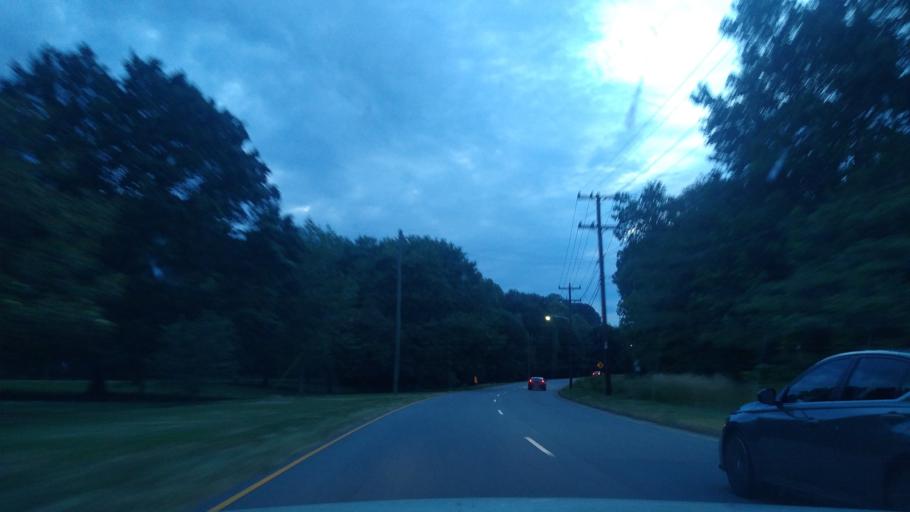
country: US
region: North Carolina
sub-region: Guilford County
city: Greensboro
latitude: 36.1059
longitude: -79.8027
